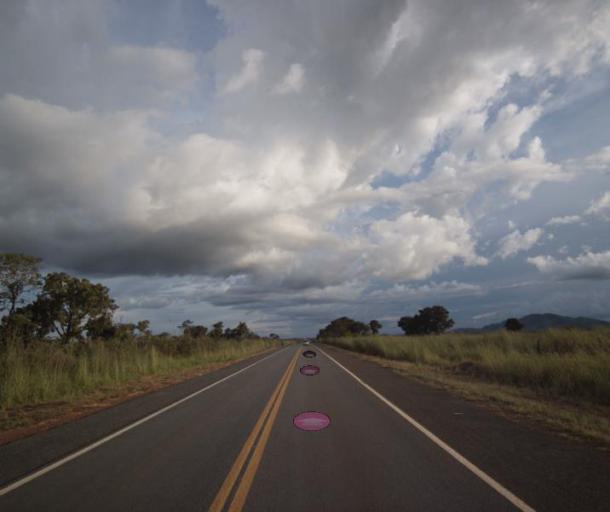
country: BR
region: Goias
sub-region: Barro Alto
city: Barro Alto
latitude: -14.8389
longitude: -48.6383
